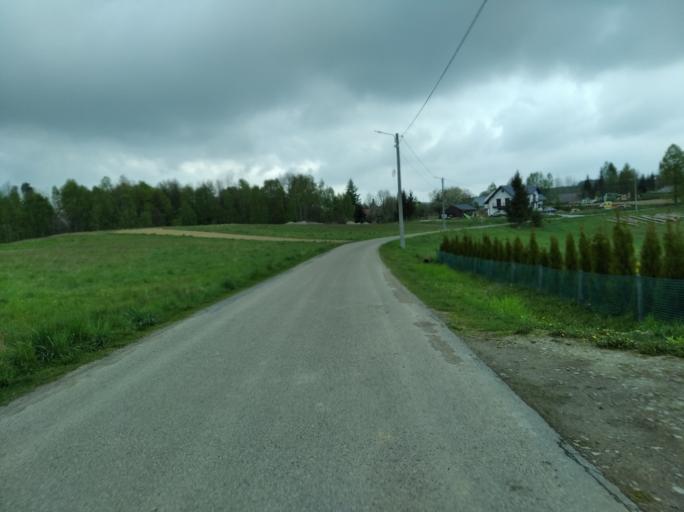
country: PL
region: Subcarpathian Voivodeship
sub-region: Powiat brzozowski
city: Golcowa
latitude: 49.7558
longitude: 22.0584
